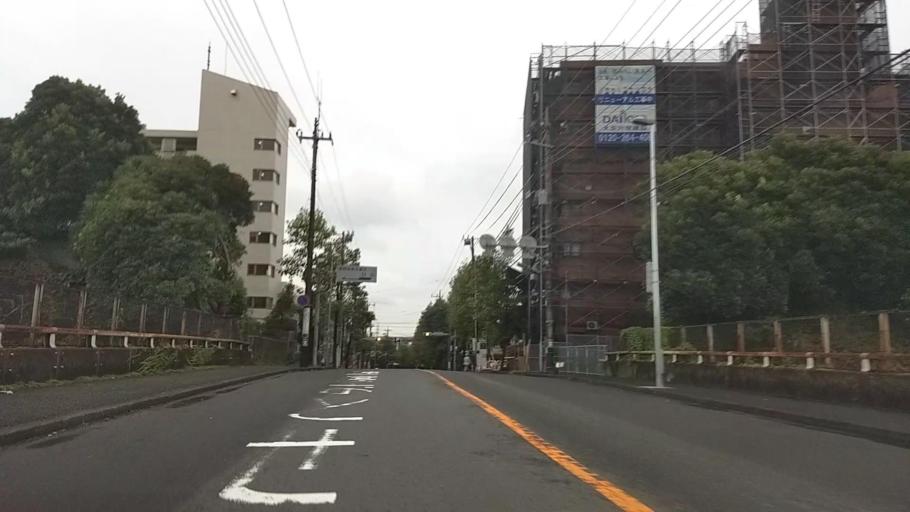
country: JP
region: Kanagawa
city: Kamakura
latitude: 35.3880
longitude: 139.5763
